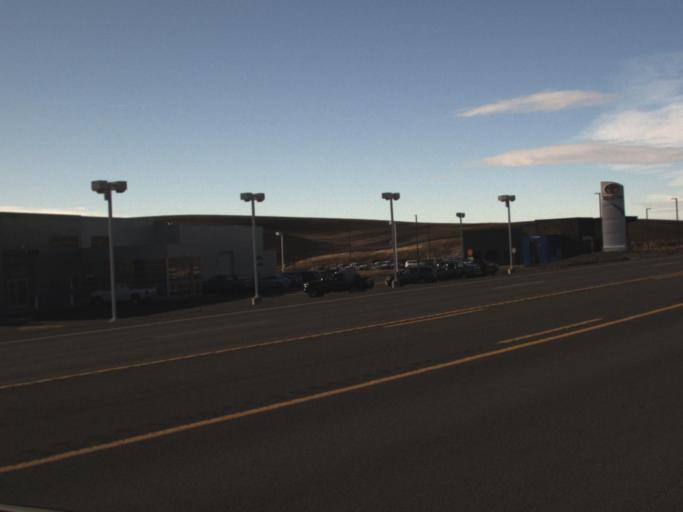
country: US
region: Idaho
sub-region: Latah County
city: Moscow
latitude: 46.7388
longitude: -117.0609
